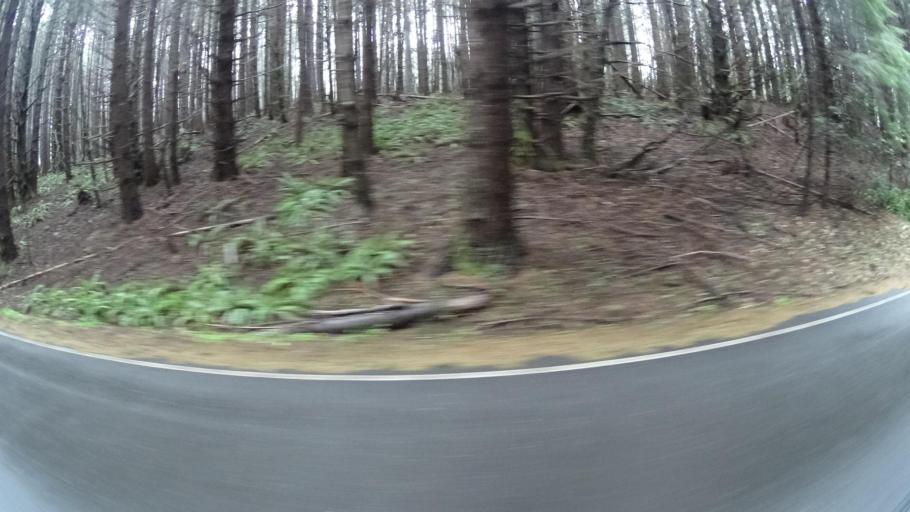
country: US
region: California
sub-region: Humboldt County
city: Westhaven-Moonstone
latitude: 41.2152
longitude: -123.9572
